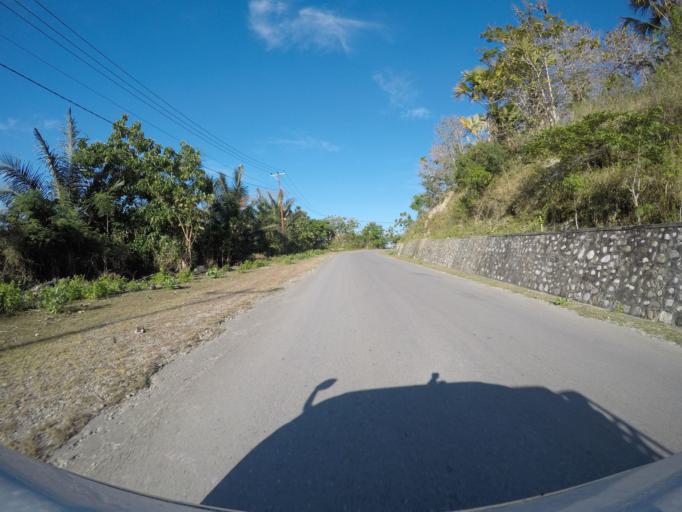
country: TL
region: Viqueque
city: Viqueque
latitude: -8.8716
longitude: 126.3527
